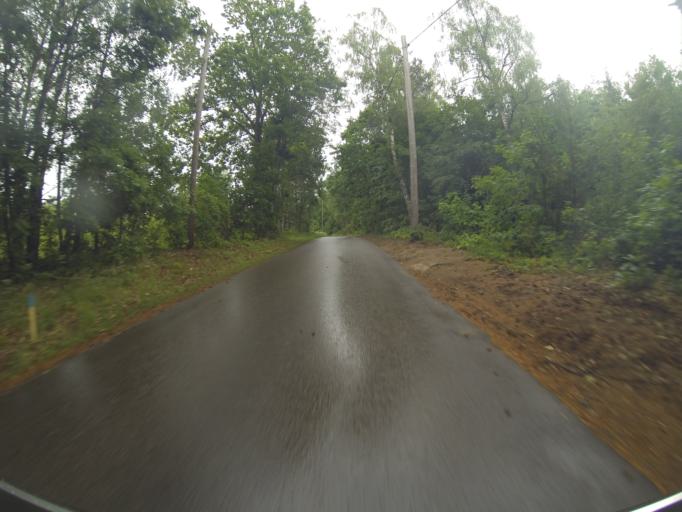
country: SE
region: Blekinge
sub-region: Ronneby Kommun
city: Ronneby
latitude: 56.1712
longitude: 15.3108
